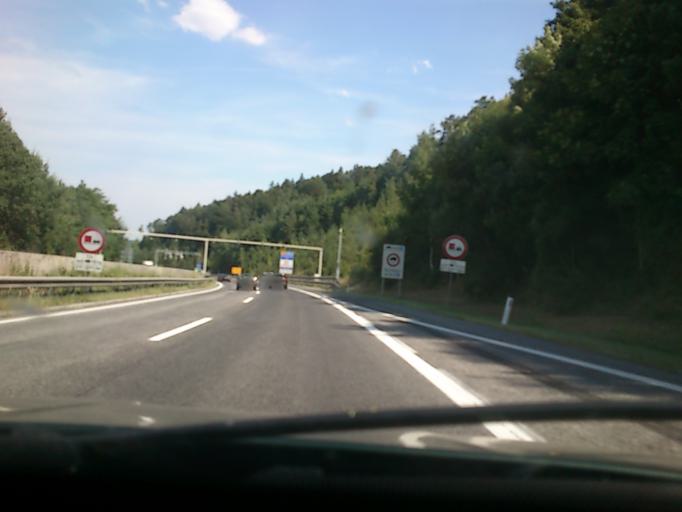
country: AT
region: Lower Austria
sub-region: Politischer Bezirk Neunkirchen
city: Grimmenstein
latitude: 47.6224
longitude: 16.1333
